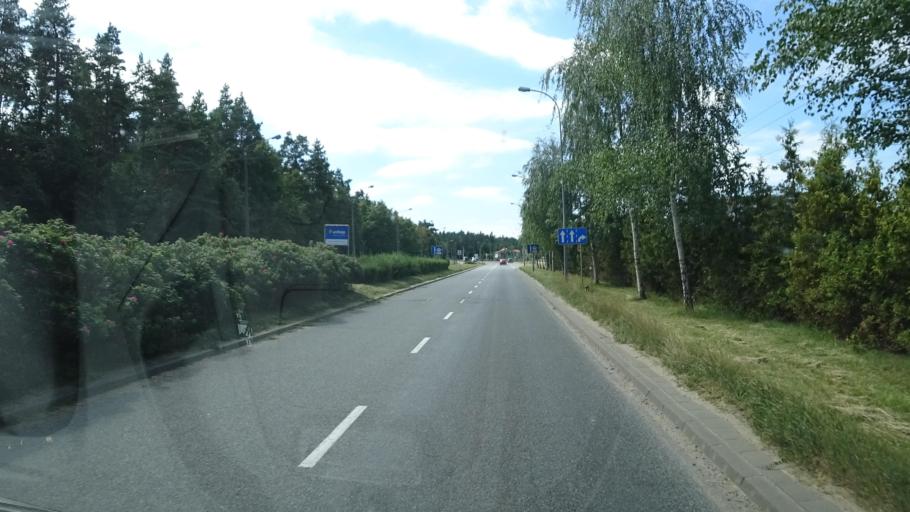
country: PL
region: Warmian-Masurian Voivodeship
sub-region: Powiat elcki
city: Elk
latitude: 53.7976
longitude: 22.3587
